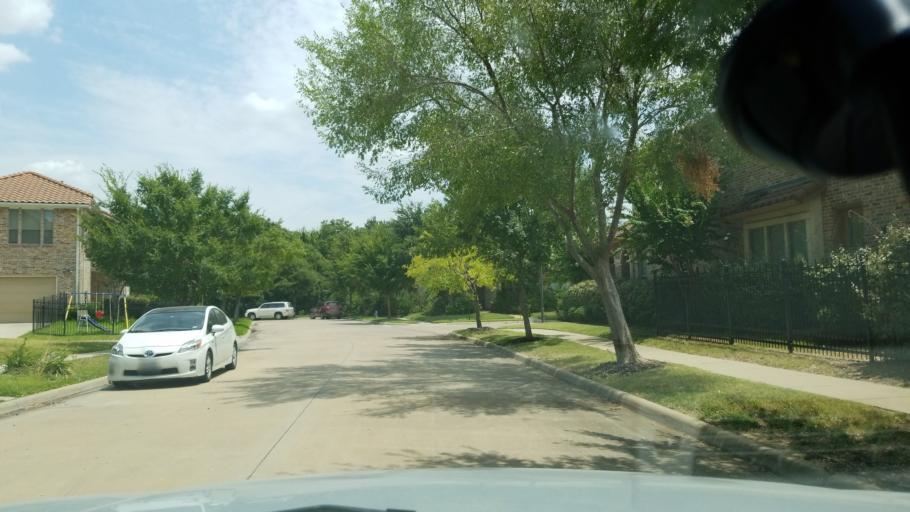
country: US
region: Texas
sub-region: Dallas County
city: Farmers Branch
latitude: 32.9019
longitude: -96.9293
